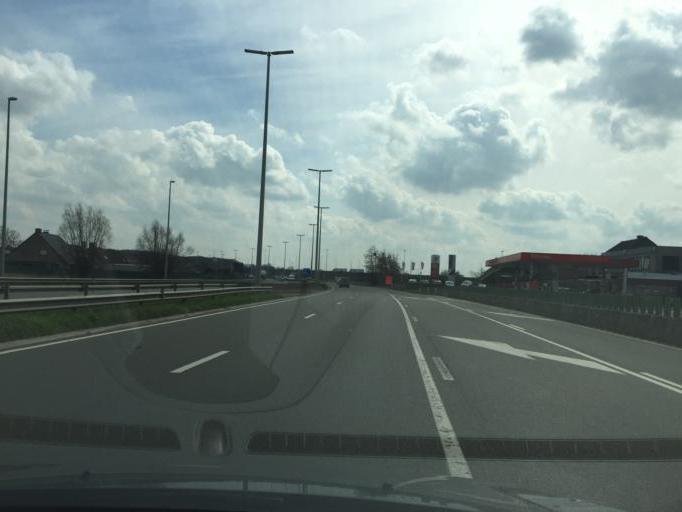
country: BE
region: Flanders
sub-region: Provincie Oost-Vlaanderen
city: Aalter
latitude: 51.0806
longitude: 3.4452
